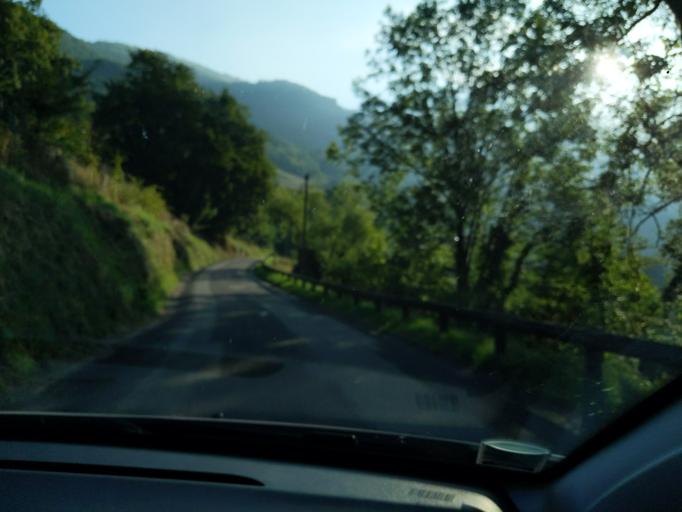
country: FR
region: Rhone-Alpes
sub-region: Departement de la Savoie
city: Aiton
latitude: 45.5622
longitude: 6.2716
